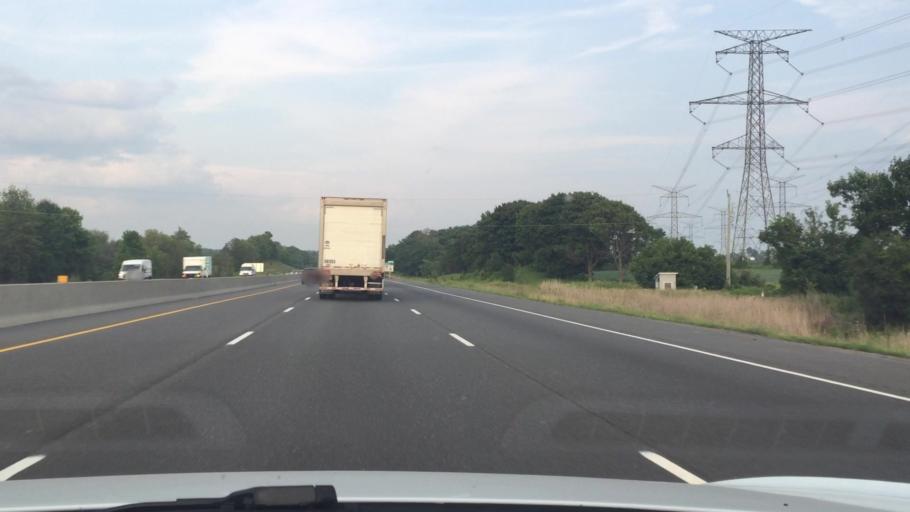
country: CA
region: Ontario
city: Cobourg
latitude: 43.9352
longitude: -78.4699
